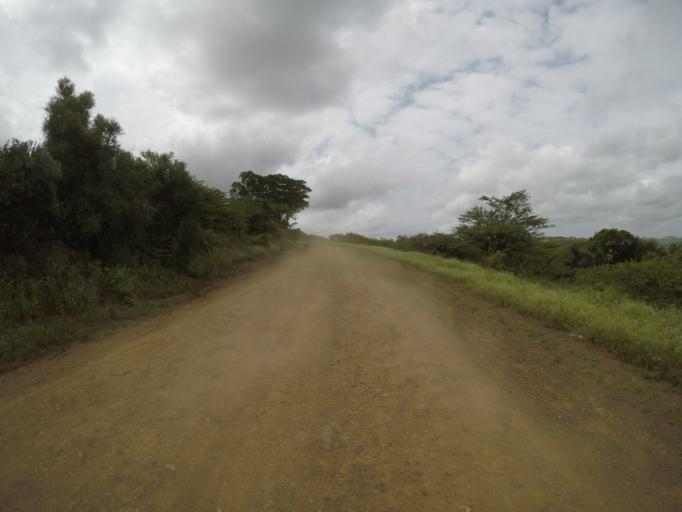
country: ZA
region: KwaZulu-Natal
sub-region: uThungulu District Municipality
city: Empangeni
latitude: -28.6077
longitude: 31.8949
